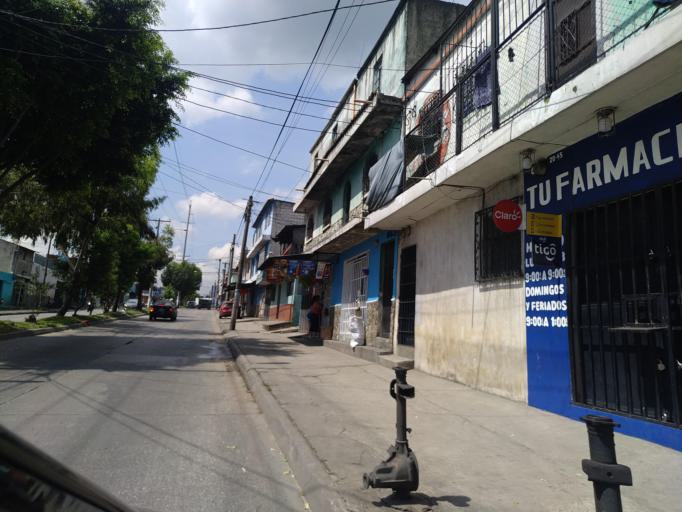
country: GT
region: Guatemala
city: Mixco
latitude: 14.6657
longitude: -90.5851
